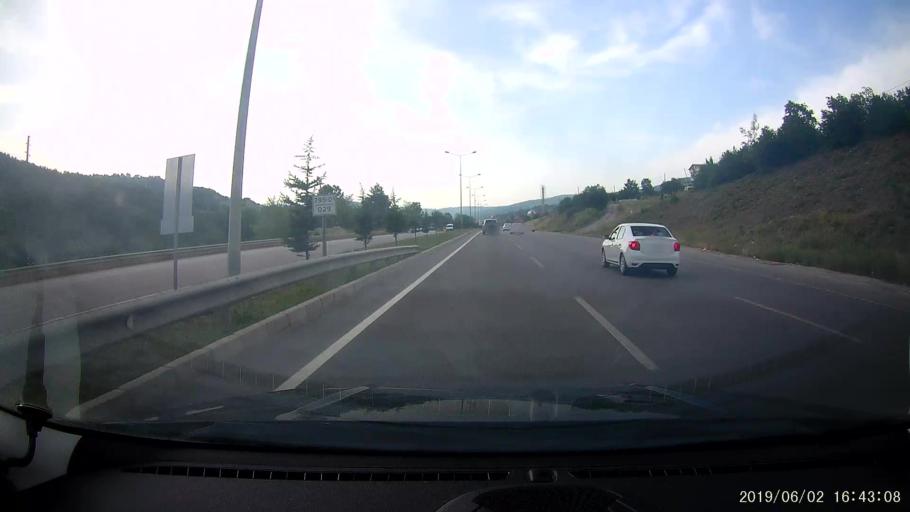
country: TR
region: Samsun
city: Kavak
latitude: 41.1303
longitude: 36.1333
